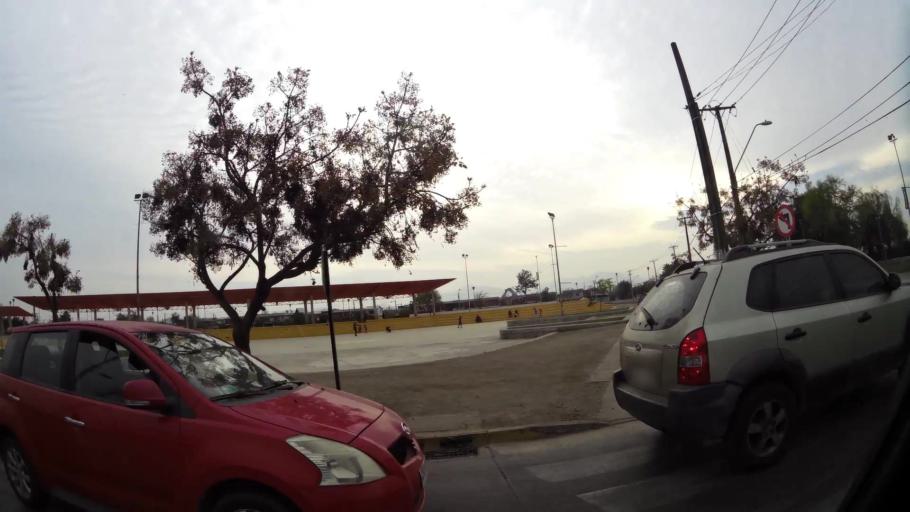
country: CL
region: Santiago Metropolitan
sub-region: Provincia de Santiago
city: Lo Prado
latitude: -33.5121
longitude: -70.7778
